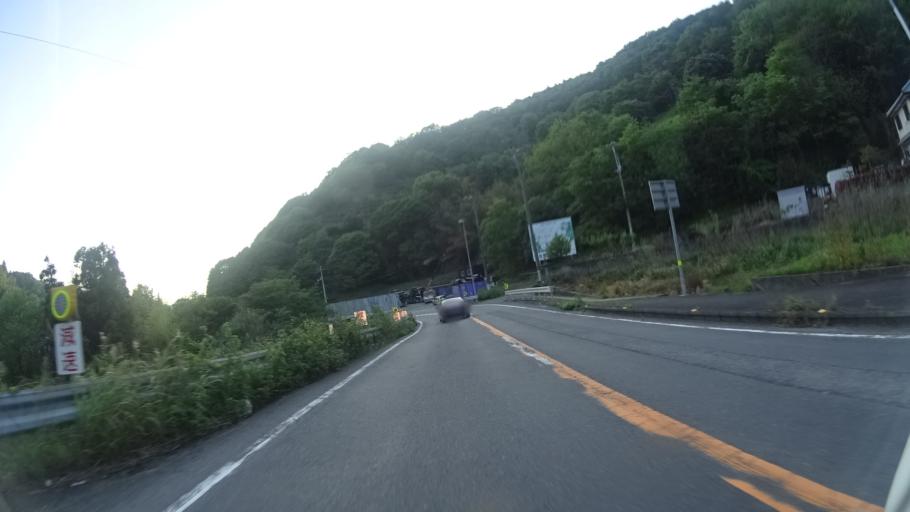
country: JP
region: Ehime
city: Kawanoecho
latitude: 33.9910
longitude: 133.6410
